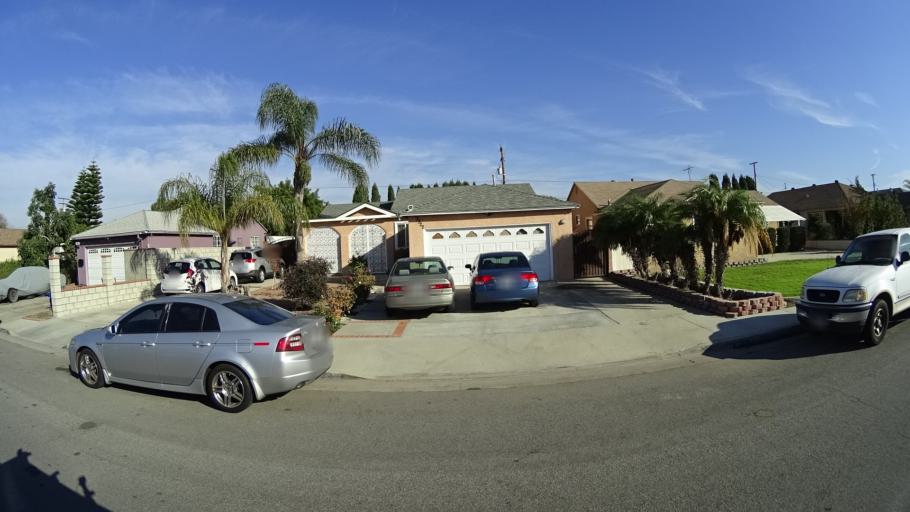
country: US
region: California
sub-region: Orange County
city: Westminster
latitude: 33.7690
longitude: -117.9839
